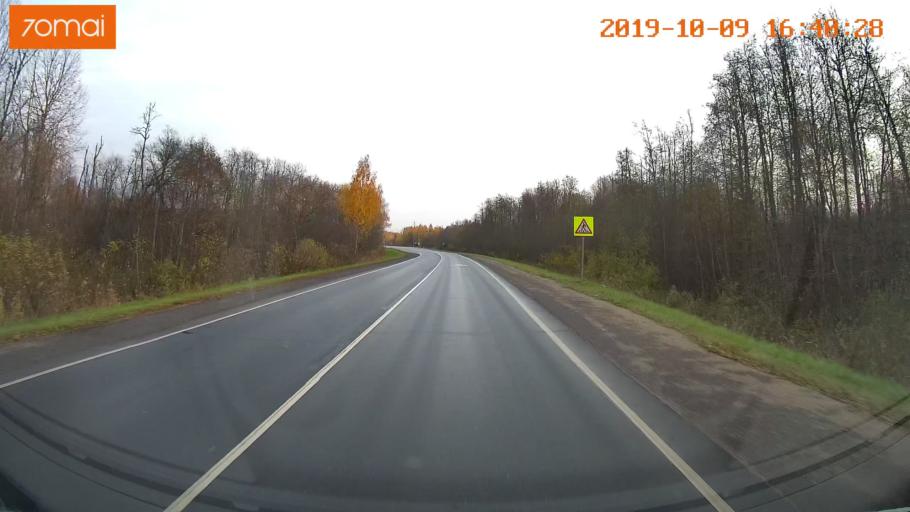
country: RU
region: Kostroma
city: Volgorechensk
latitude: 57.4831
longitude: 41.0614
